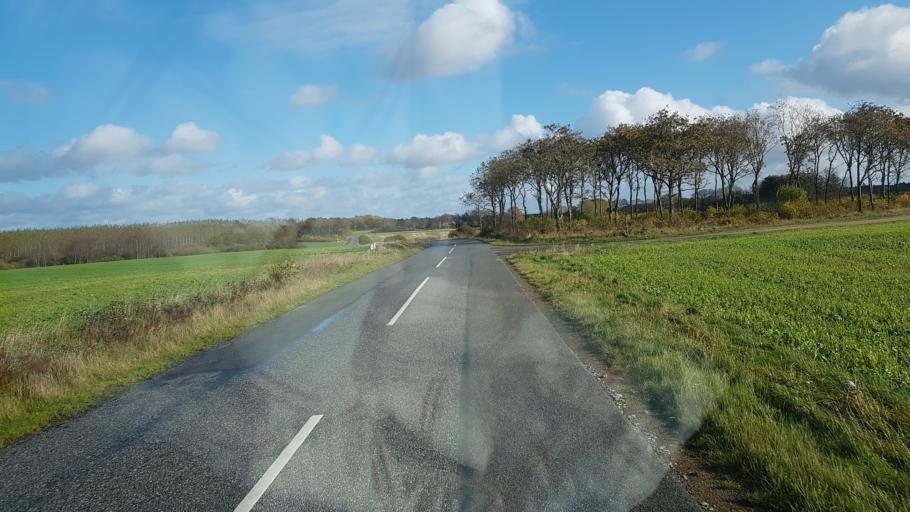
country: DK
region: South Denmark
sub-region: Varde Kommune
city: Olgod
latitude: 55.6921
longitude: 8.6968
